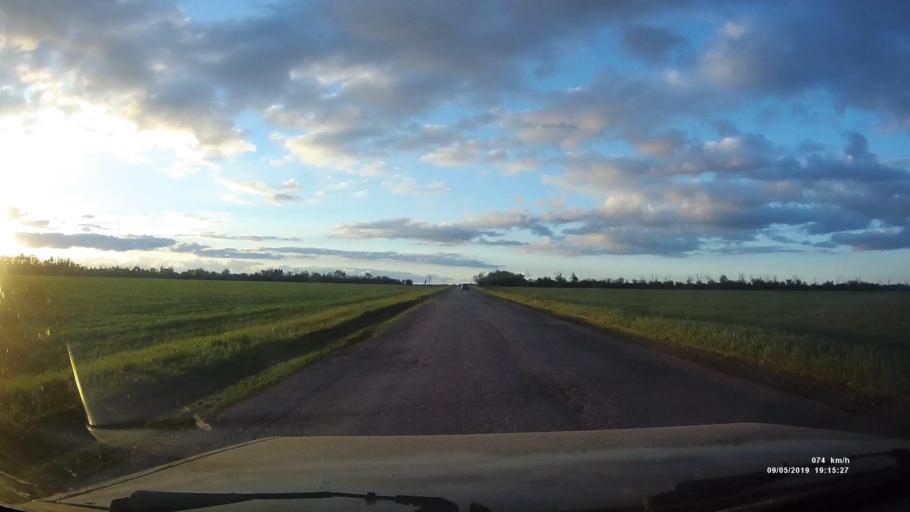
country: RU
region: Krasnodarskiy
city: Kanelovskaya
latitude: 46.7681
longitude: 39.2120
